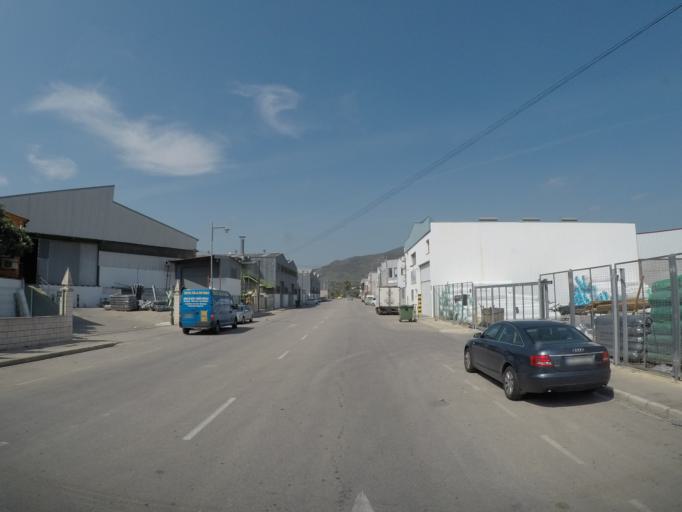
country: ES
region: Valencia
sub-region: Provincia de Alicante
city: Pego
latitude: 38.8467
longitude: -0.1122
